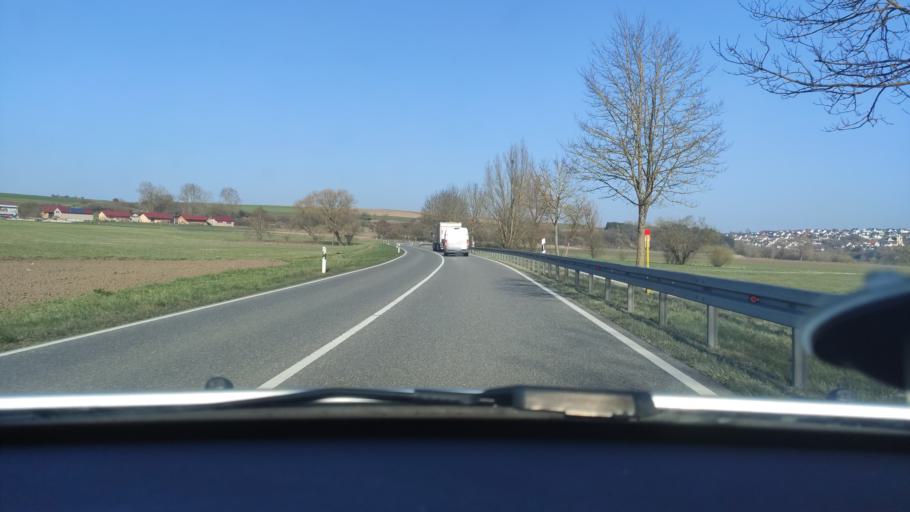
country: DE
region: Baden-Wuerttemberg
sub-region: Tuebingen Region
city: Haigerloch
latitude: 48.3427
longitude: 8.8296
